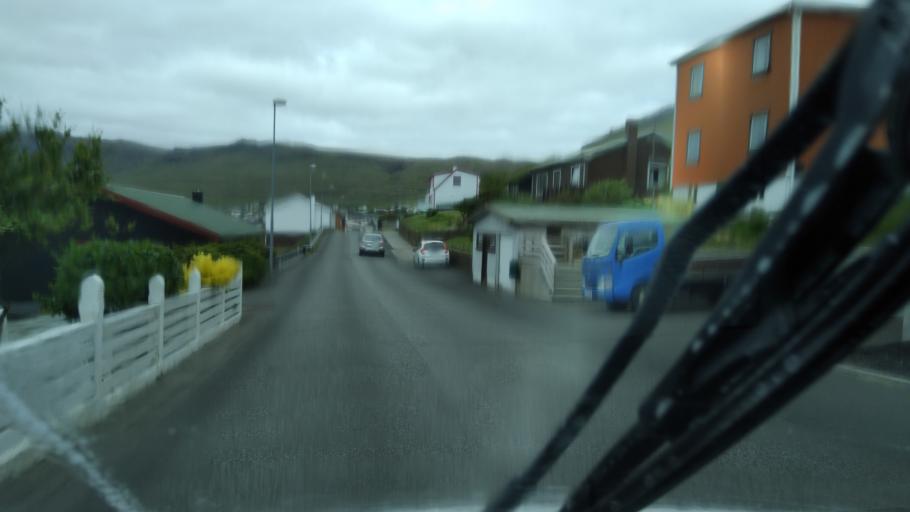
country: FO
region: Suduroy
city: Tvoroyri
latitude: 61.5570
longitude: -6.8186
